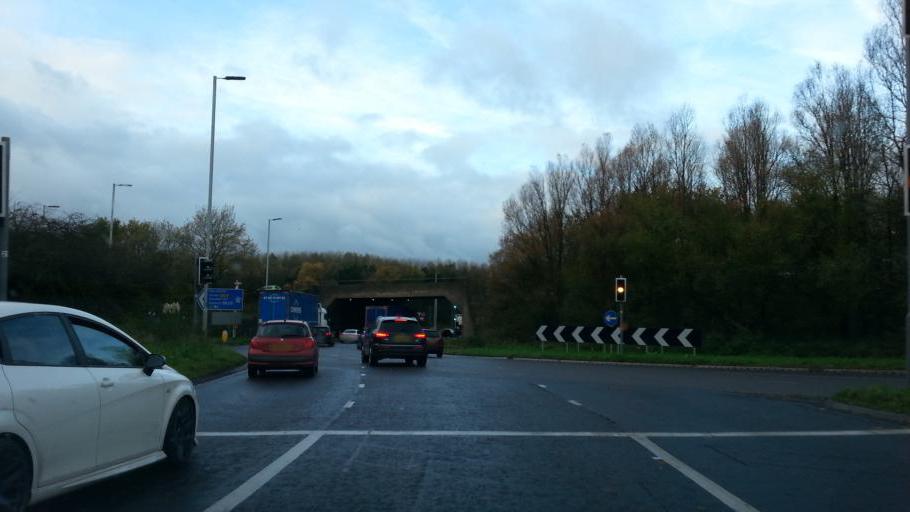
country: GB
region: England
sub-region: Leicestershire
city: Markfield
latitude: 52.6957
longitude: -1.2906
